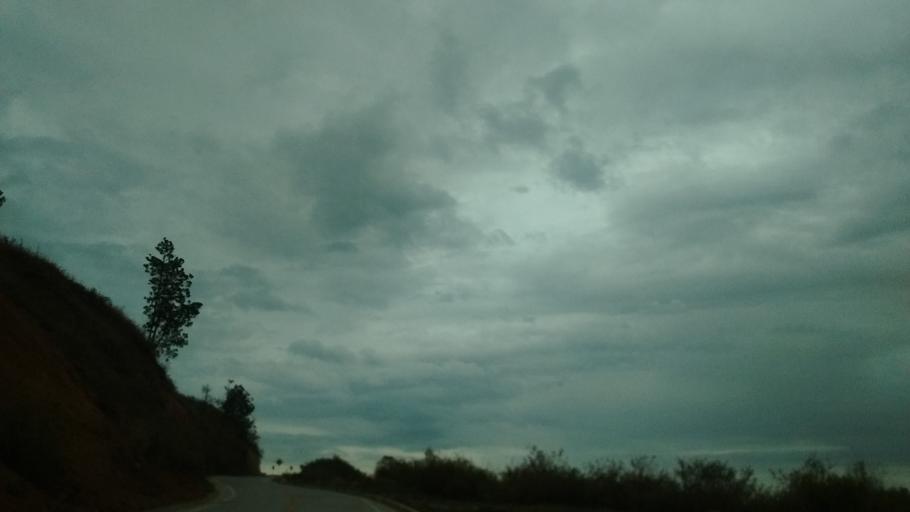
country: CO
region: Cauca
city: La Sierra
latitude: 2.1499
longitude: -76.7787
